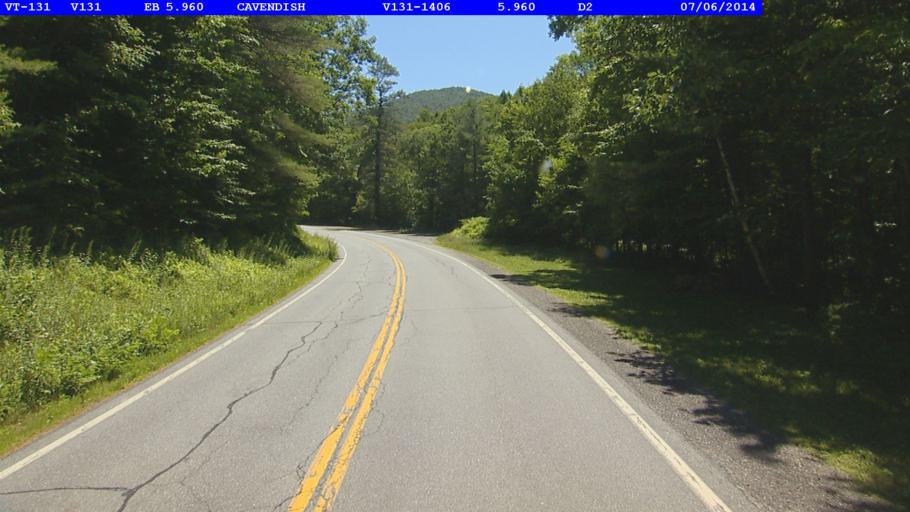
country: US
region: Vermont
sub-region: Windsor County
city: Springfield
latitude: 43.3903
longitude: -72.5668
